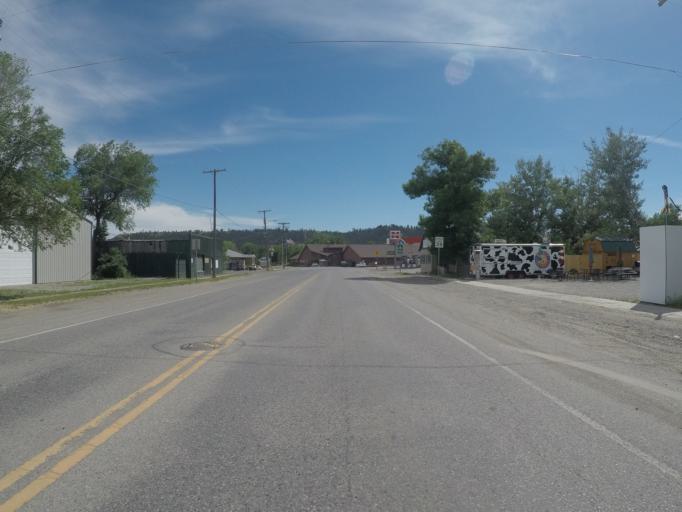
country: US
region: Montana
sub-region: Stillwater County
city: Columbus
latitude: 45.6356
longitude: -109.2530
